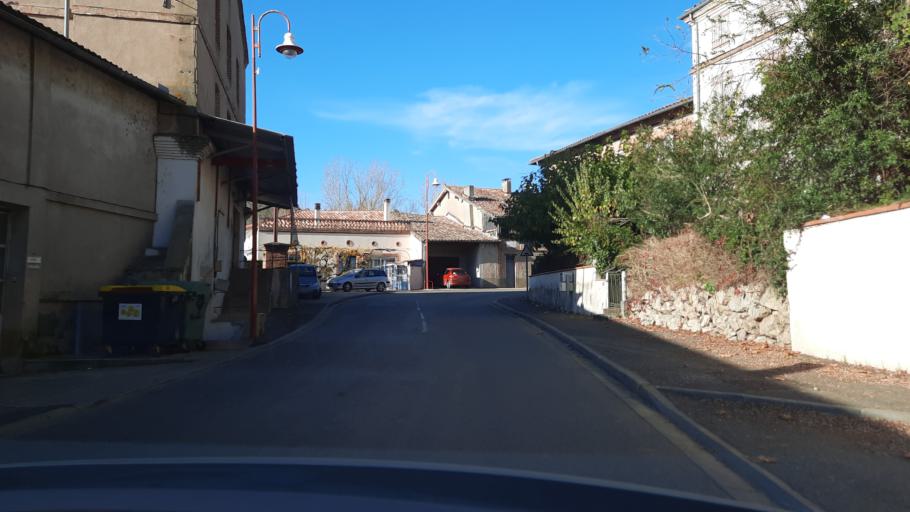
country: FR
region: Midi-Pyrenees
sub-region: Departement du Tarn-et-Garonne
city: Montauban
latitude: 44.0900
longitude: 1.3472
